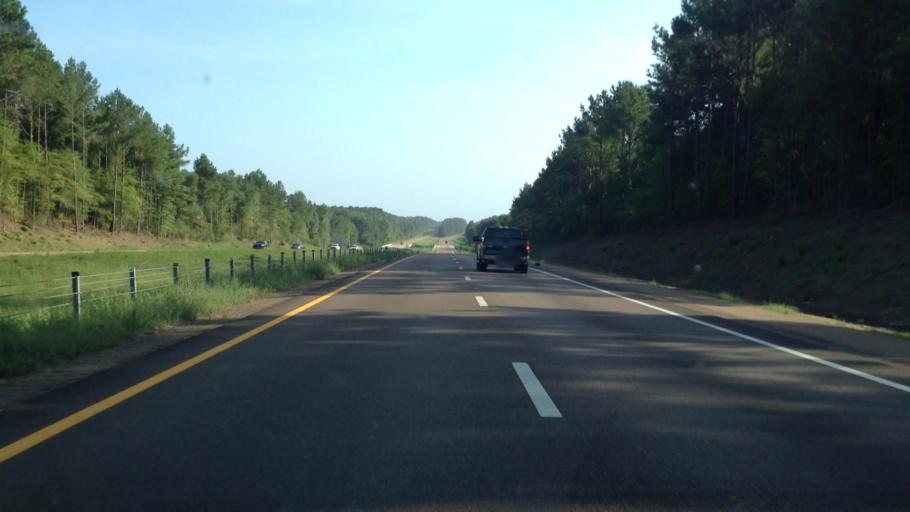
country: US
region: Mississippi
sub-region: Pike County
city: Summit
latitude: 31.4322
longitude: -90.4797
